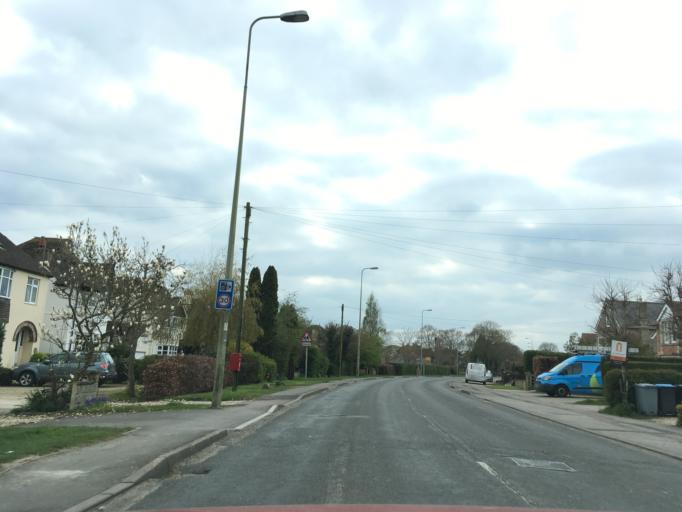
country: GB
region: England
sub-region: Oxfordshire
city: Witney
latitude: 51.7943
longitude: -1.4701
